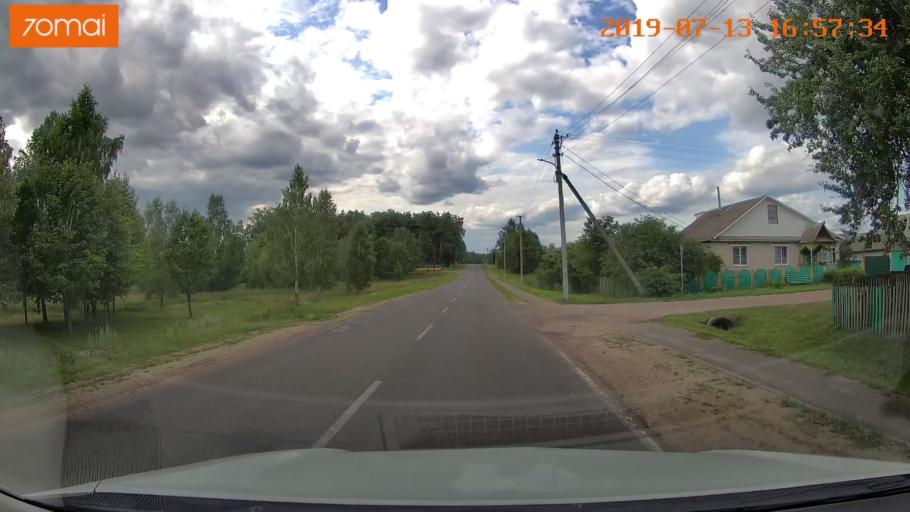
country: BY
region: Mogilev
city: Kirawsk
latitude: 53.2810
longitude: 29.4503
